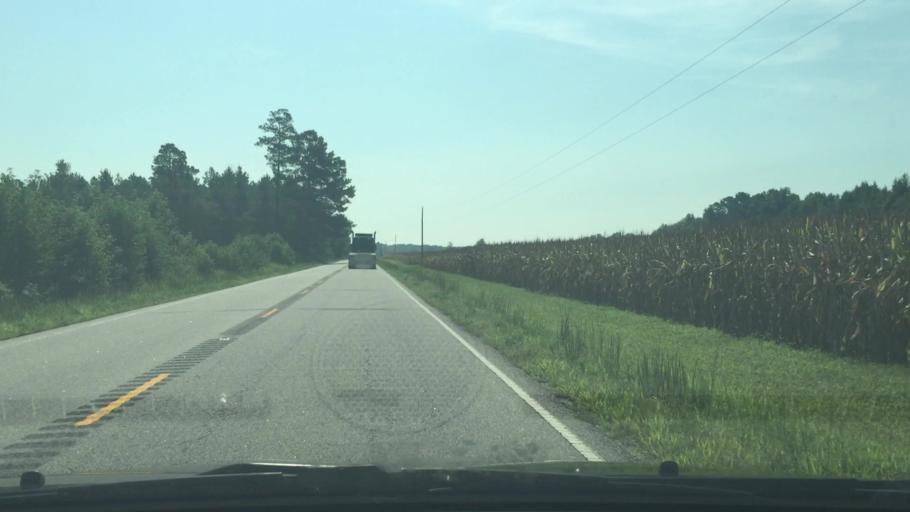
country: US
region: Virginia
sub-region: Sussex County
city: Sussex
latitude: 36.9818
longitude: -77.2385
